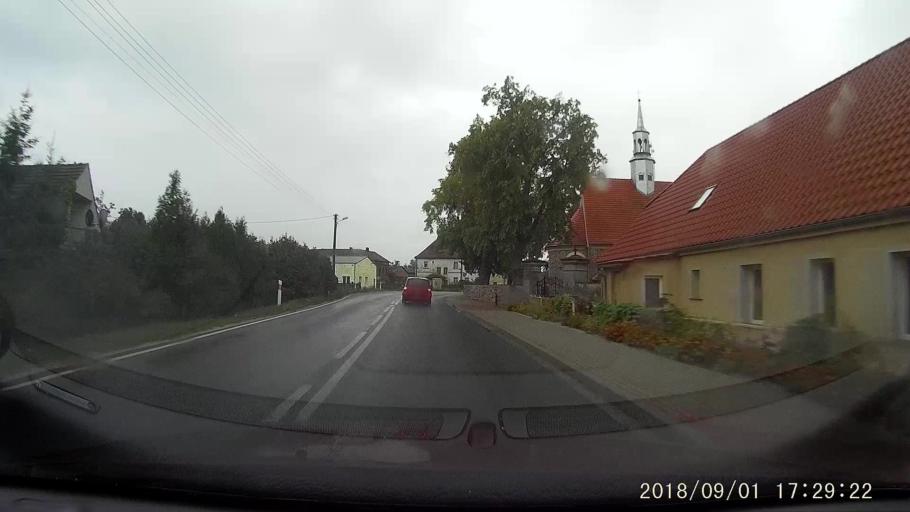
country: PL
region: Lubusz
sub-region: Powiat zaganski
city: Zagan
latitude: 51.6510
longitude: 15.3165
